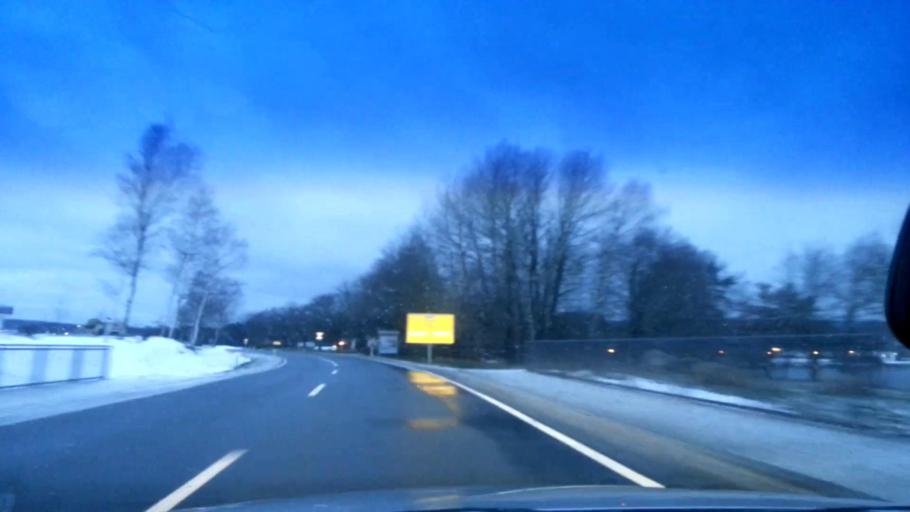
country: DE
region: Bavaria
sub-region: Upper Franconia
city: Weissenstadt
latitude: 50.0954
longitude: 11.8742
